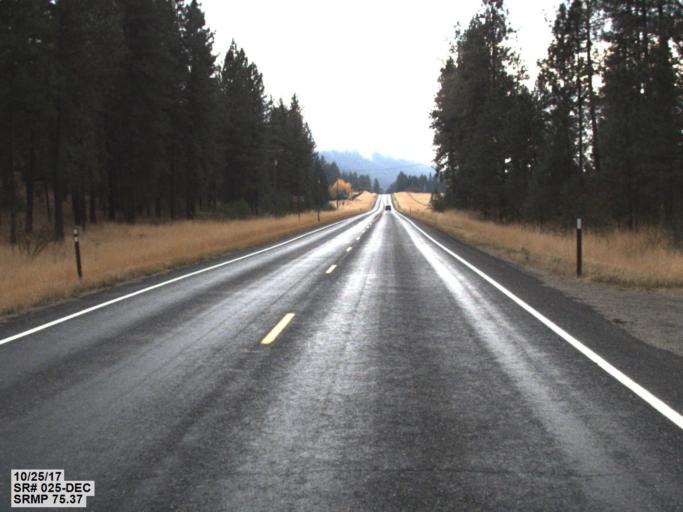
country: US
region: Washington
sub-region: Stevens County
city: Kettle Falls
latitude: 48.5459
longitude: -118.1290
